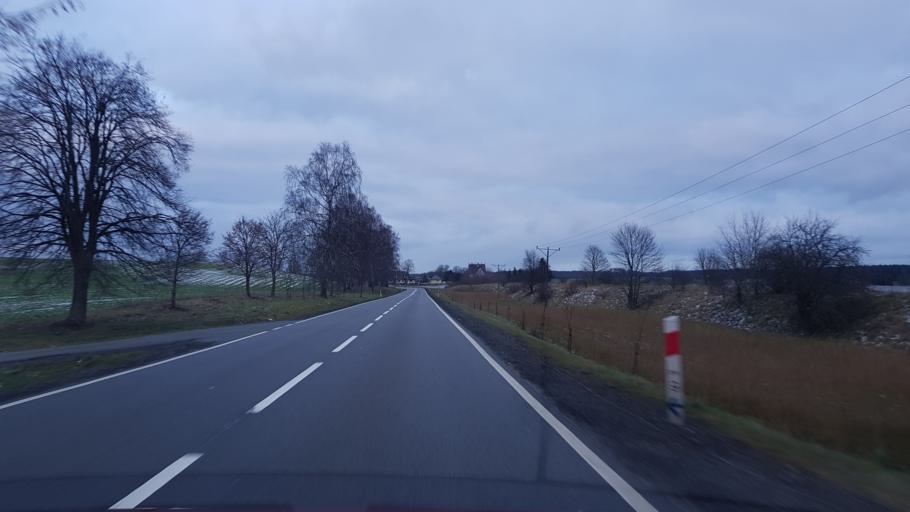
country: PL
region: Pomeranian Voivodeship
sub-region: Powiat bytowski
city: Tuchomie
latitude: 54.0507
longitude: 17.2292
